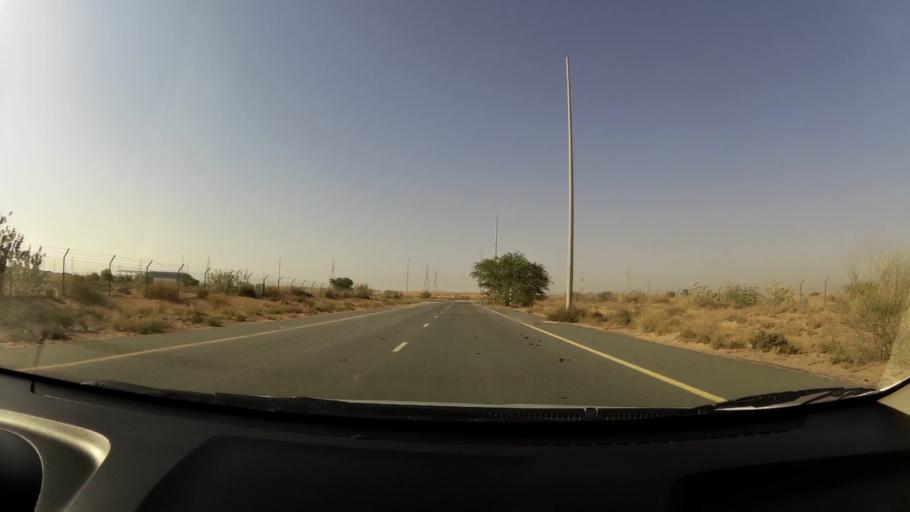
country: AE
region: Umm al Qaywayn
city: Umm al Qaywayn
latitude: 25.4358
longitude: 55.5945
